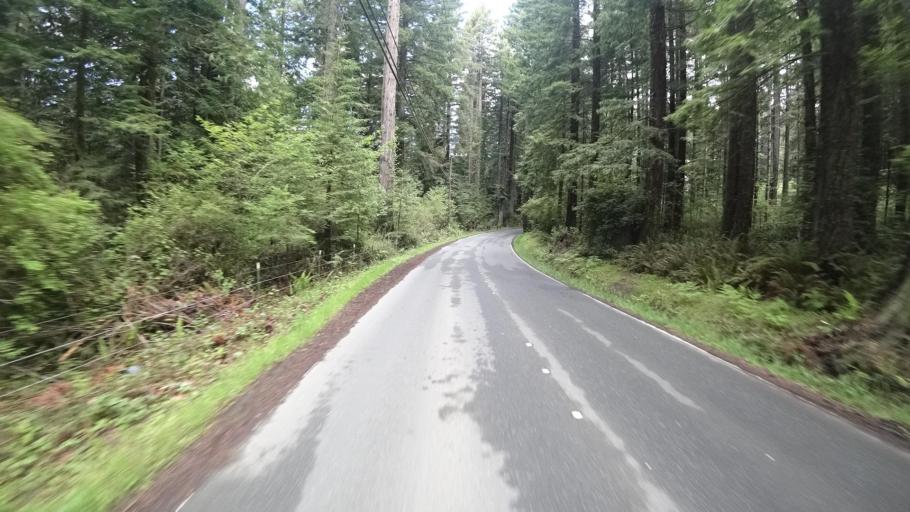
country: US
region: California
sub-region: Humboldt County
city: Blue Lake
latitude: 40.9141
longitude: -124.0235
